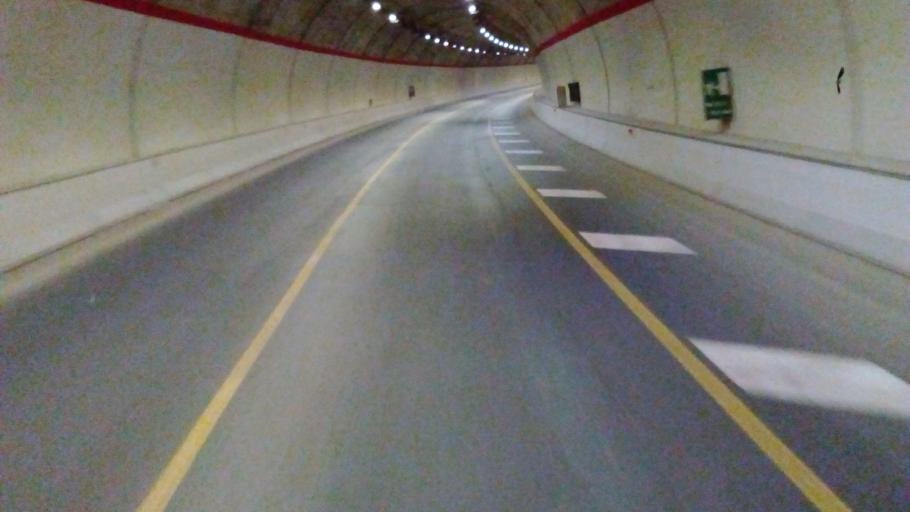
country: IT
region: Tuscany
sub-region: Provincia di Grosseto
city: Civitella Marittima
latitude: 43.0368
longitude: 11.2767
